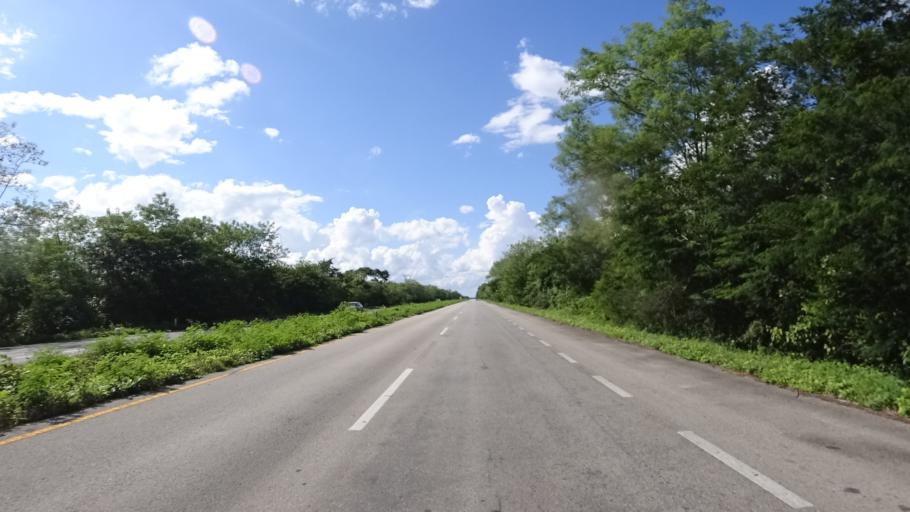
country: MX
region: Yucatan
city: Hoctun
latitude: 20.8450
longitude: -89.1646
